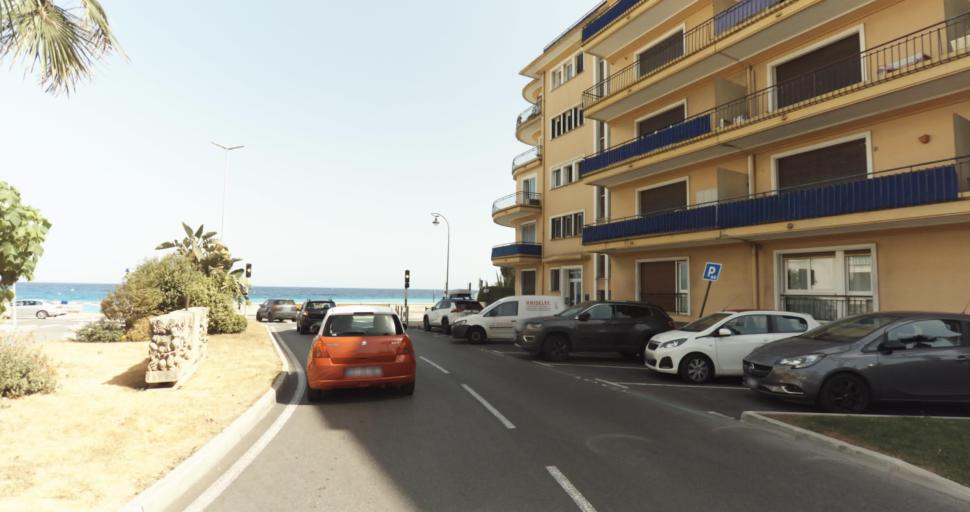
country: FR
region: Provence-Alpes-Cote d'Azur
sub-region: Departement des Alpes-Maritimes
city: Roquebrune-Cap-Martin
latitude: 43.7657
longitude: 7.4876
